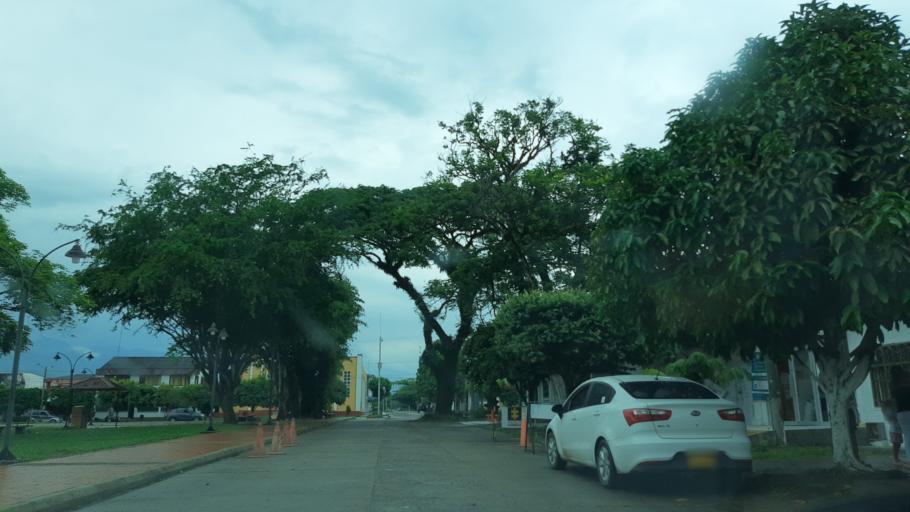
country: CO
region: Casanare
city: Monterrey
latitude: 4.8750
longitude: -72.8929
